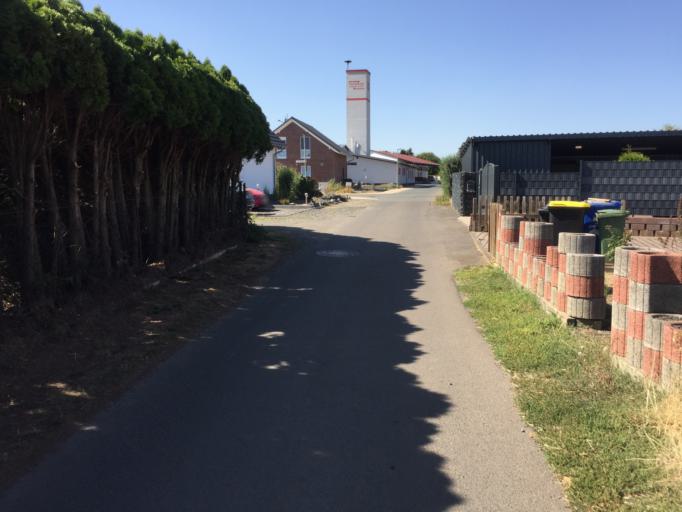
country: DE
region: Hesse
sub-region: Regierungsbezirk Giessen
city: Hungen
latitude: 50.4353
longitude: 8.8871
